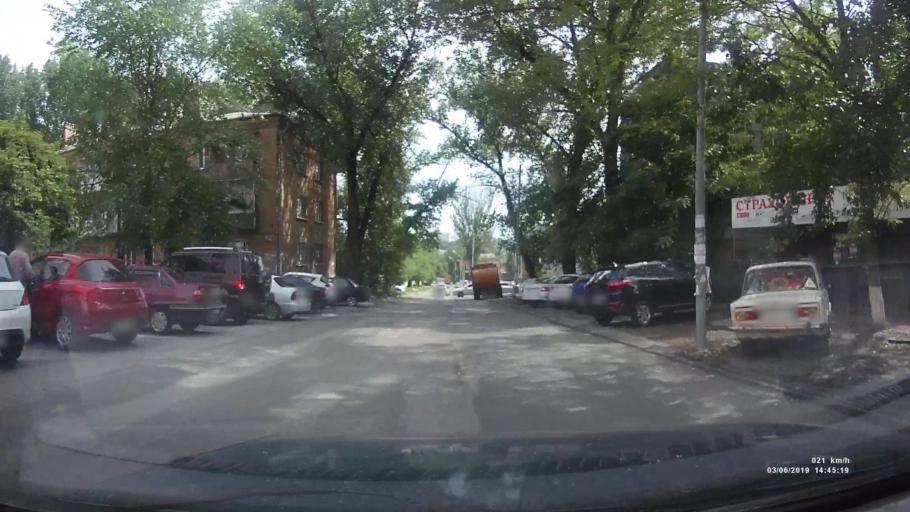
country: RU
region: Rostov
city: Rostov-na-Donu
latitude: 47.2490
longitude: 39.7231
